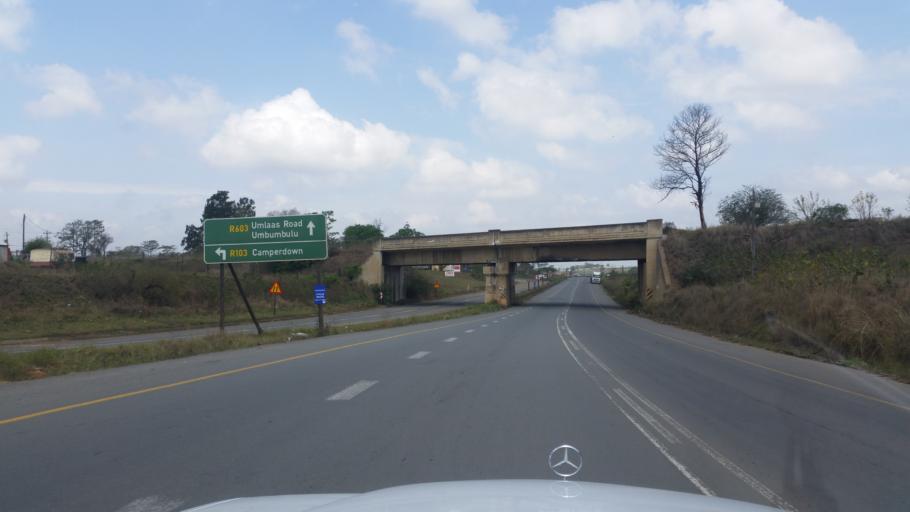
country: ZA
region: KwaZulu-Natal
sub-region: uMgungundlovu District Municipality
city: Camperdown
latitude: -29.7221
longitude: 30.4983
